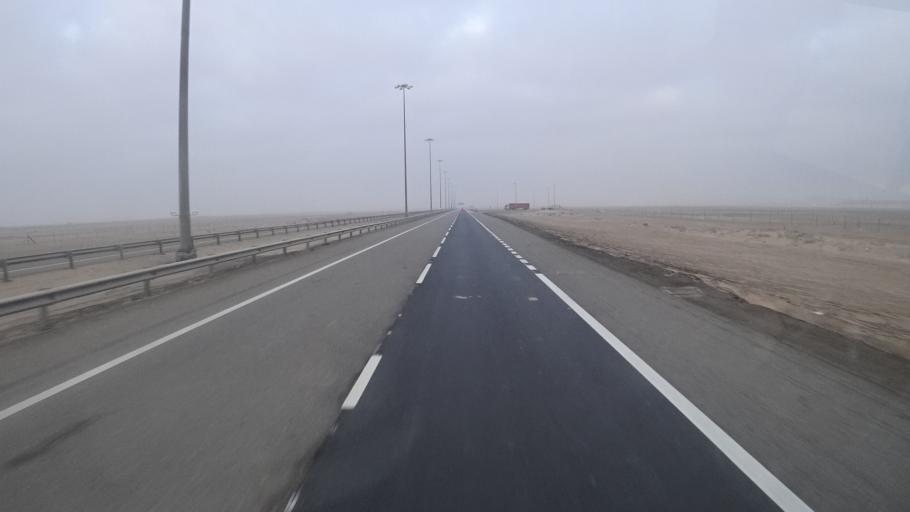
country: AE
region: Abu Dhabi
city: Abu Dhabi
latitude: 24.2512
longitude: 54.6681
